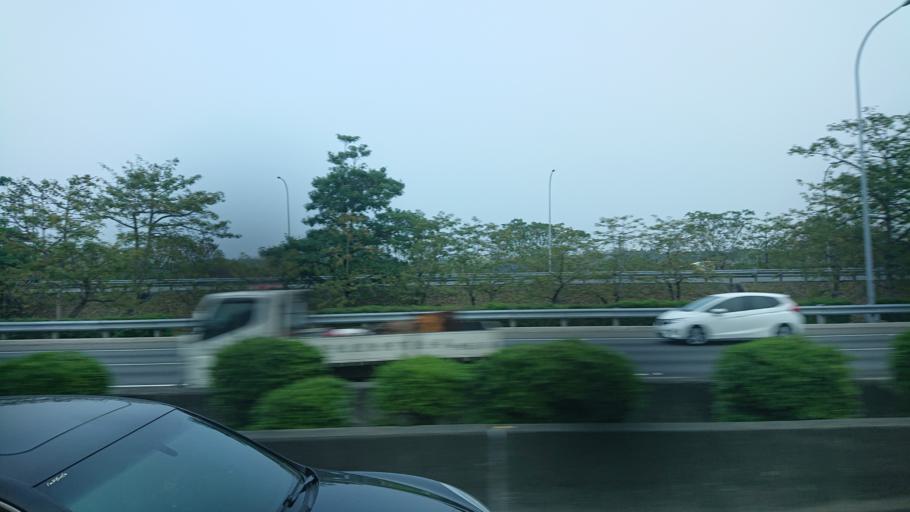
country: TW
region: Taiwan
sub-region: Yunlin
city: Douliu
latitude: 23.8725
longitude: 120.4901
